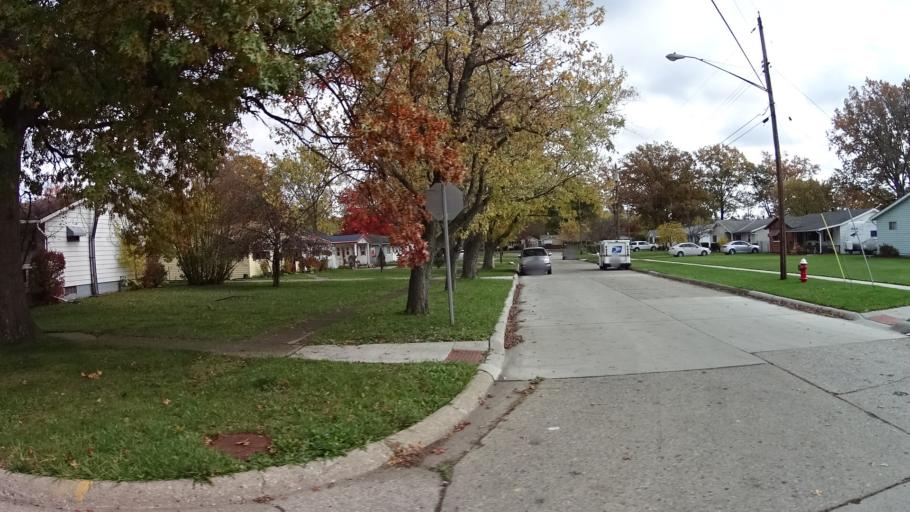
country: US
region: Ohio
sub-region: Lorain County
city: Sheffield
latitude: 41.4349
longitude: -82.1273
